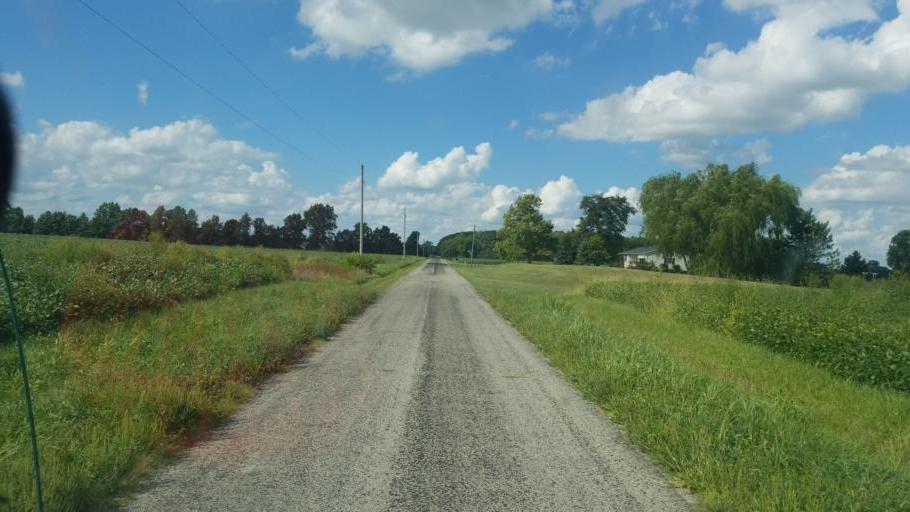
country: US
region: Ohio
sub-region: Union County
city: Richwood
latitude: 40.4572
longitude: -83.3419
